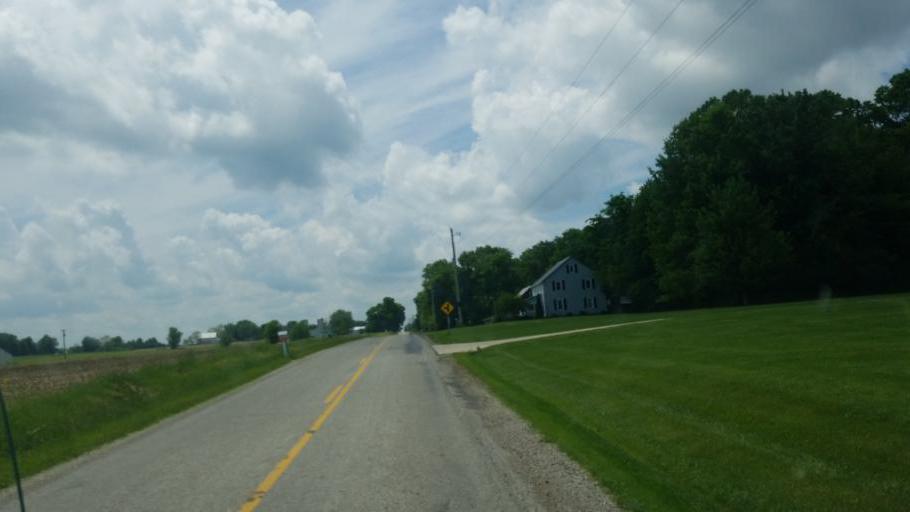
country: US
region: Ohio
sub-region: Ashland County
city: Ashland
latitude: 40.8060
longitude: -82.3224
